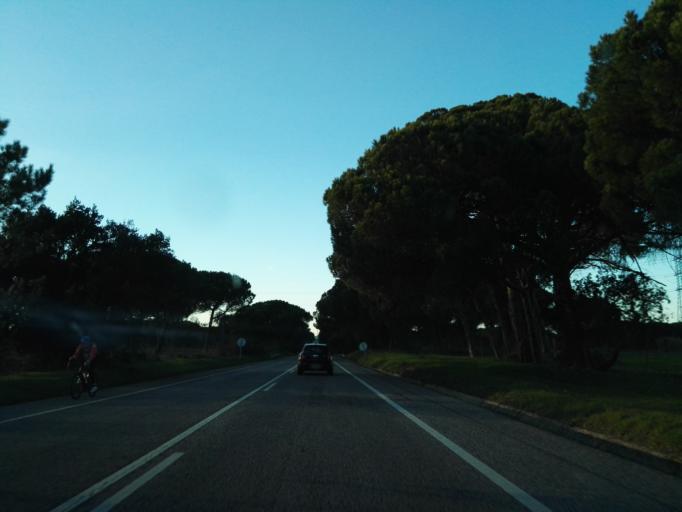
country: PT
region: Santarem
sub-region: Benavente
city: Samora Correia
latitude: 38.8924
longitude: -8.8318
